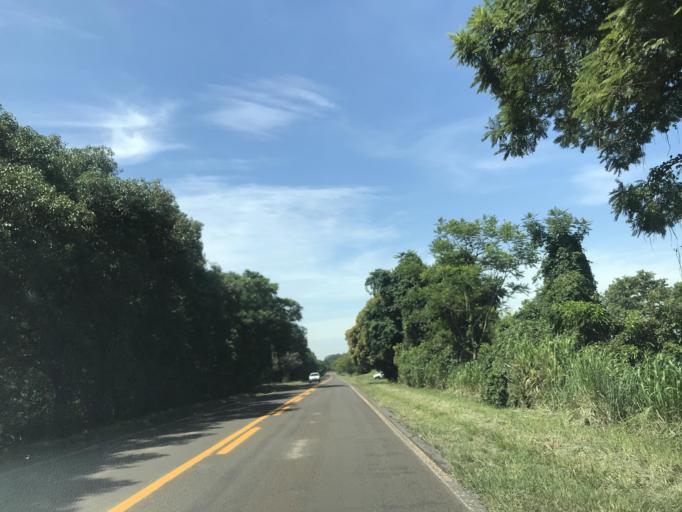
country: BR
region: Parana
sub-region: Terra Rica
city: Terra Rica
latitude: -22.7872
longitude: -52.6556
